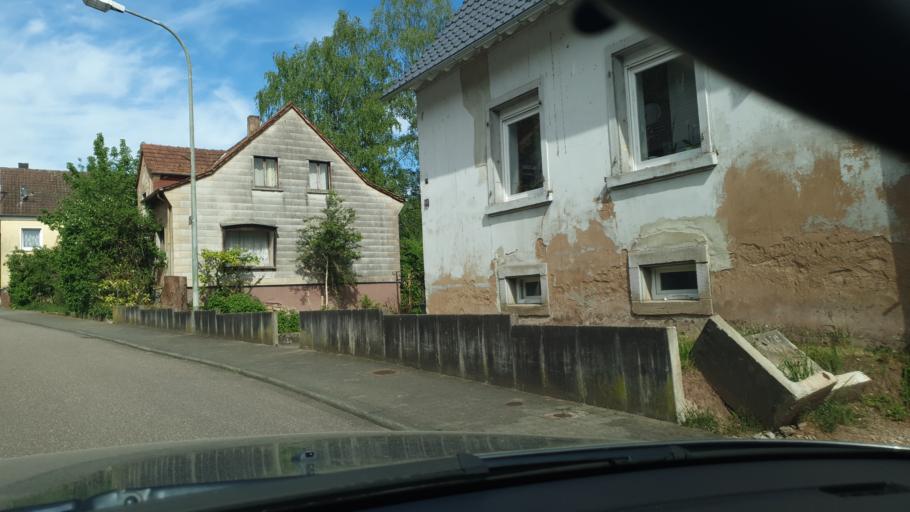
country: DE
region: Rheinland-Pfalz
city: Grossbundenbach
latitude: 49.2777
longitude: 7.4225
